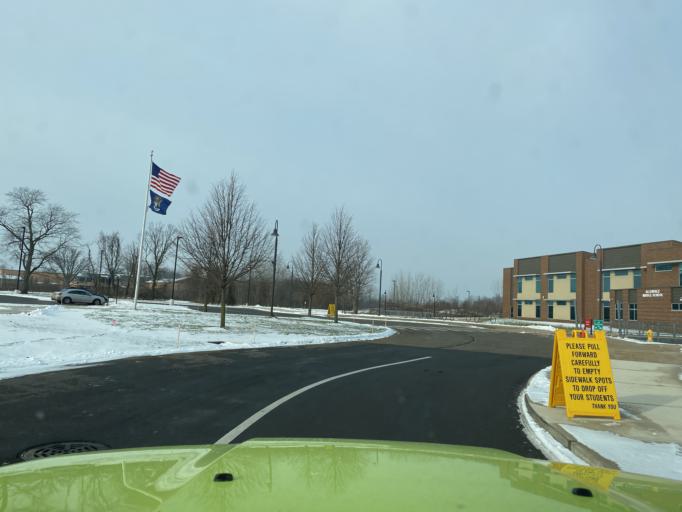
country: US
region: Michigan
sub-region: Ottawa County
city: Allendale
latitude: 42.9617
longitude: -85.9621
